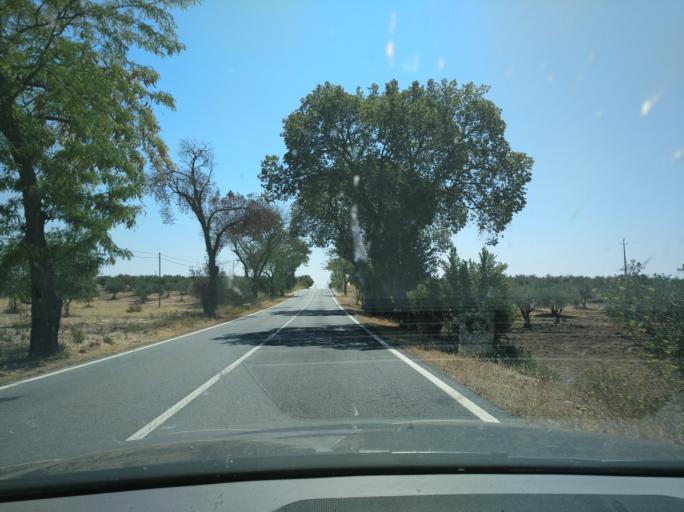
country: PT
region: Portalegre
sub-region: Campo Maior
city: Campo Maior
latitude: 38.9691
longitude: -7.0522
